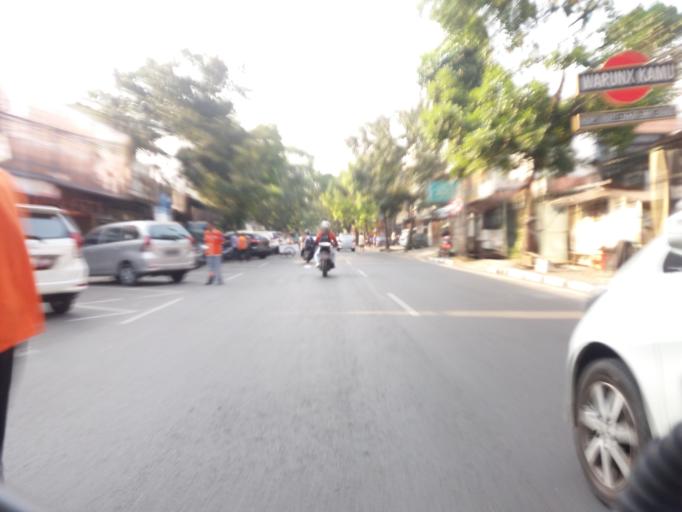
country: ID
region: West Java
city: Bandung
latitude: -6.9278
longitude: 107.6167
